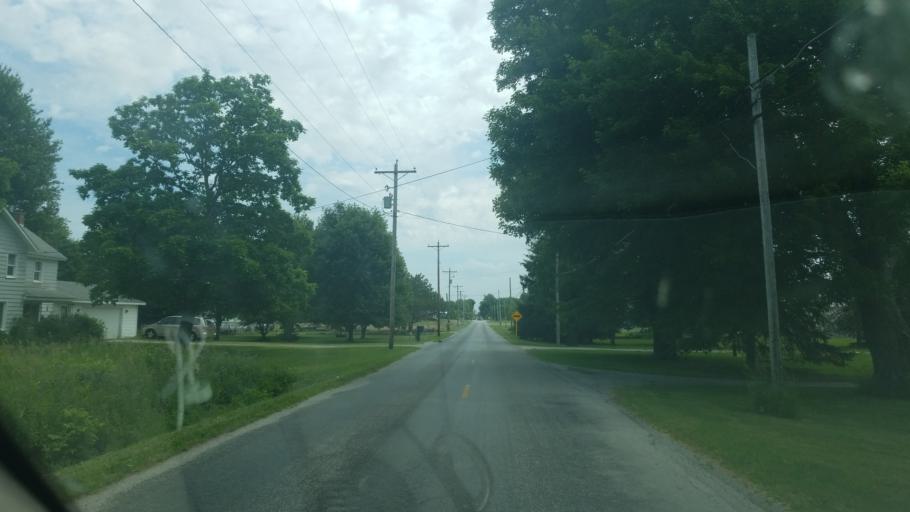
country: US
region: Ohio
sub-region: Wood County
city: Bowling Green
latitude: 41.2975
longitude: -83.6568
